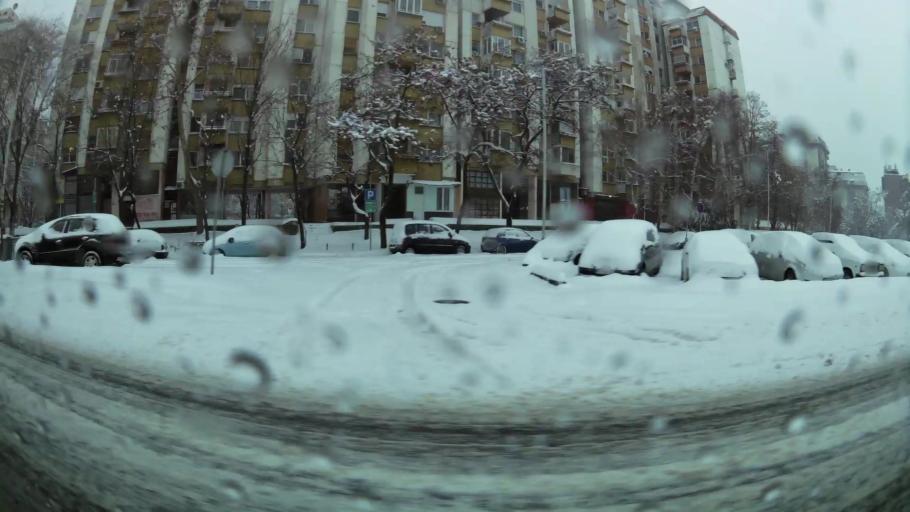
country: RS
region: Central Serbia
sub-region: Belgrade
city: Stari Grad
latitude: 44.8271
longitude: 20.4639
